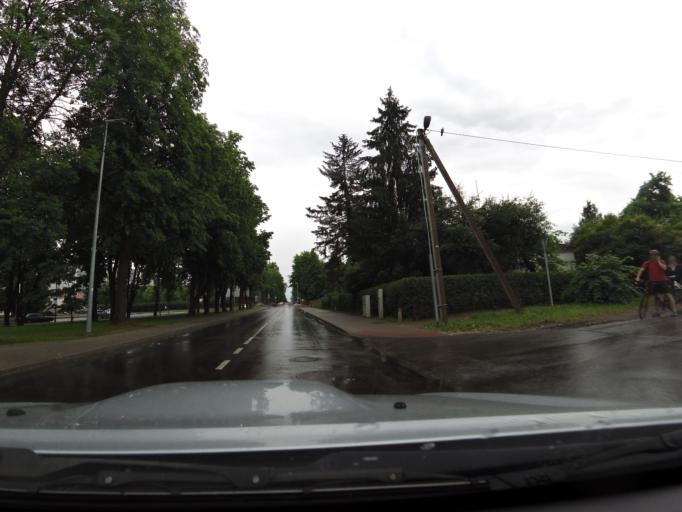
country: LT
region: Marijampoles apskritis
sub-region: Marijampole Municipality
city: Marijampole
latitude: 54.5483
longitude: 23.3468
